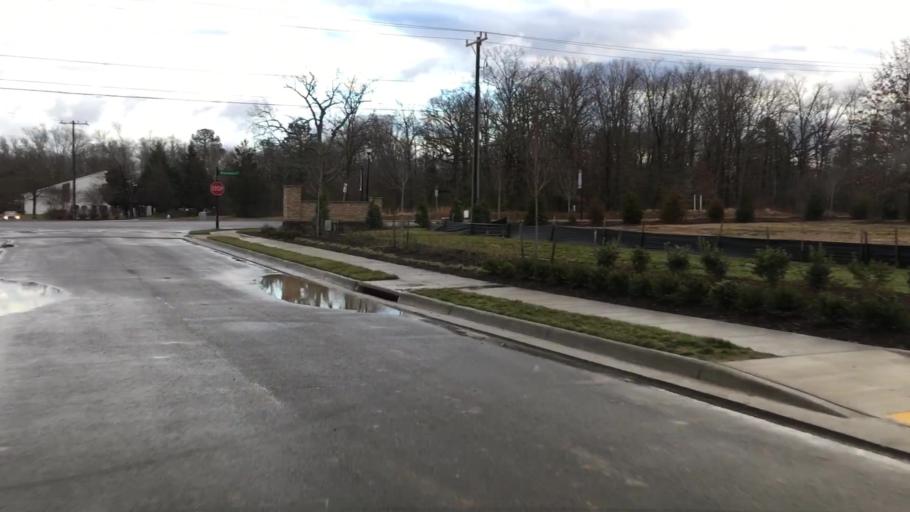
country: US
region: Virginia
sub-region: Chesterfield County
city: Bon Air
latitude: 37.4940
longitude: -77.6040
